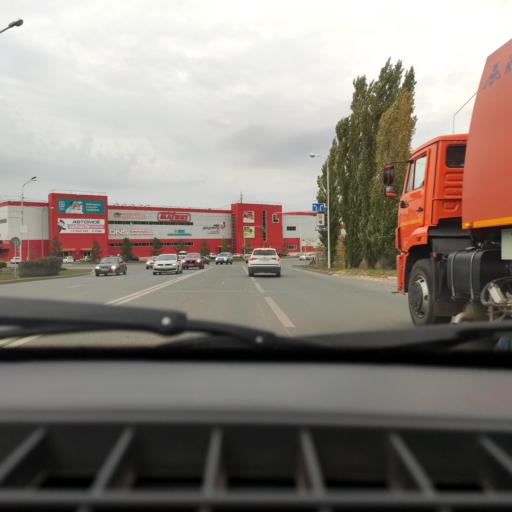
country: RU
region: Bashkortostan
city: Mikhaylovka
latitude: 54.7040
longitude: 55.8464
